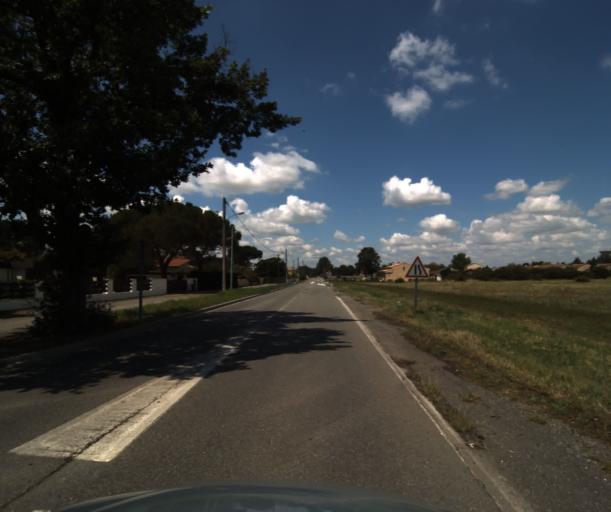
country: FR
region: Midi-Pyrenees
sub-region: Departement de la Haute-Garonne
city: Lacroix-Falgarde
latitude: 43.4960
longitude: 1.3986
